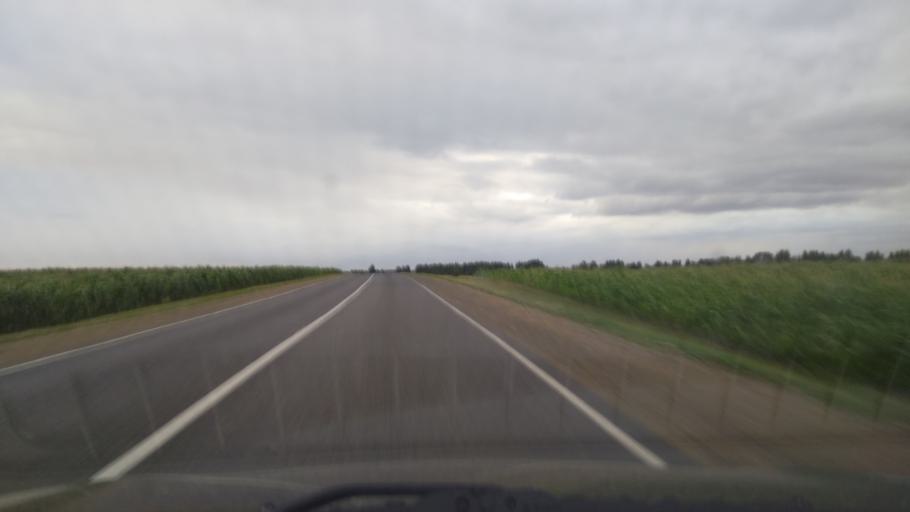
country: BY
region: Brest
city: Byaroza
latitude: 52.4327
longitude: 24.9805
